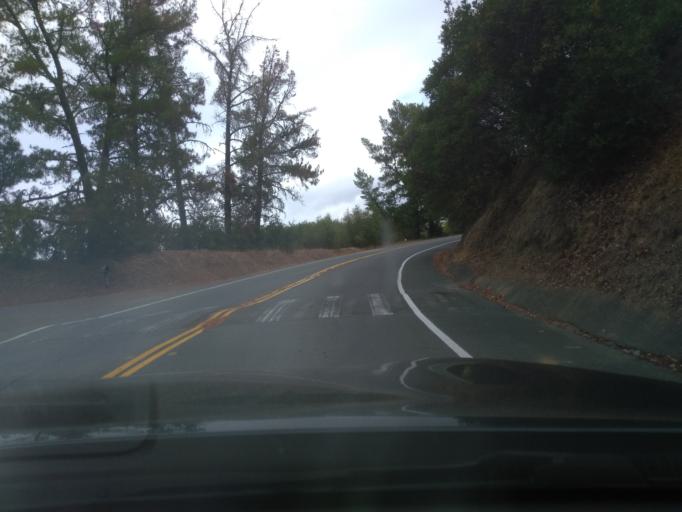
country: US
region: California
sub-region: Mendocino County
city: Ukiah
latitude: 39.2024
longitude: -123.1887
